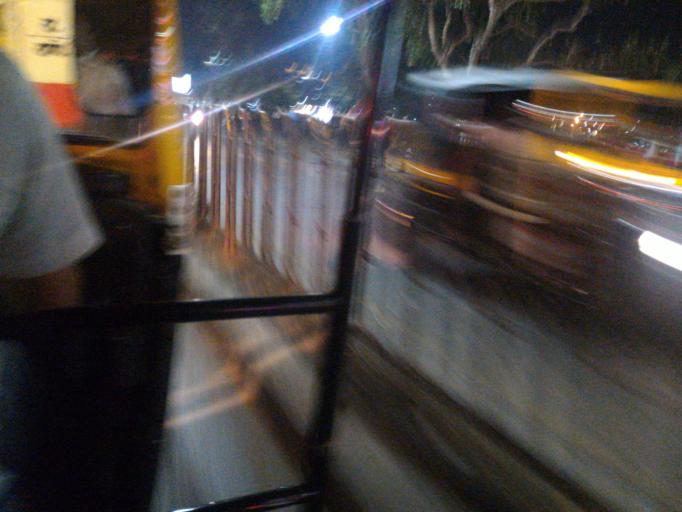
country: IN
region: Maharashtra
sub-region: Thane
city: Thane
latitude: 19.1944
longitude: 72.9769
